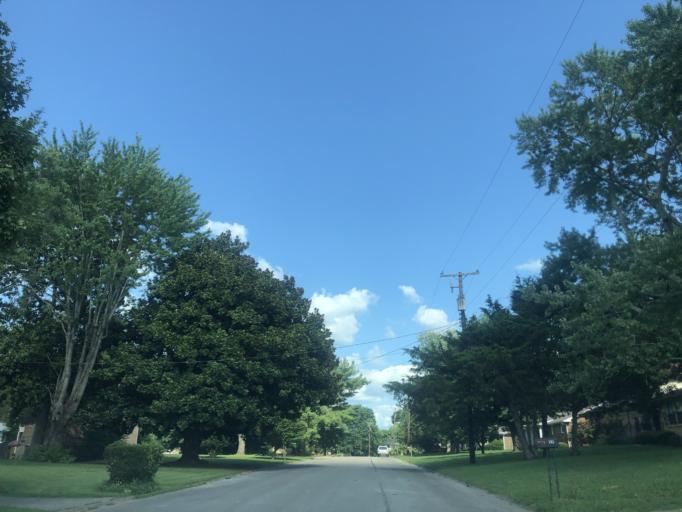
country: US
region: Tennessee
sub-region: Davidson County
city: Lakewood
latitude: 36.2066
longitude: -86.5997
